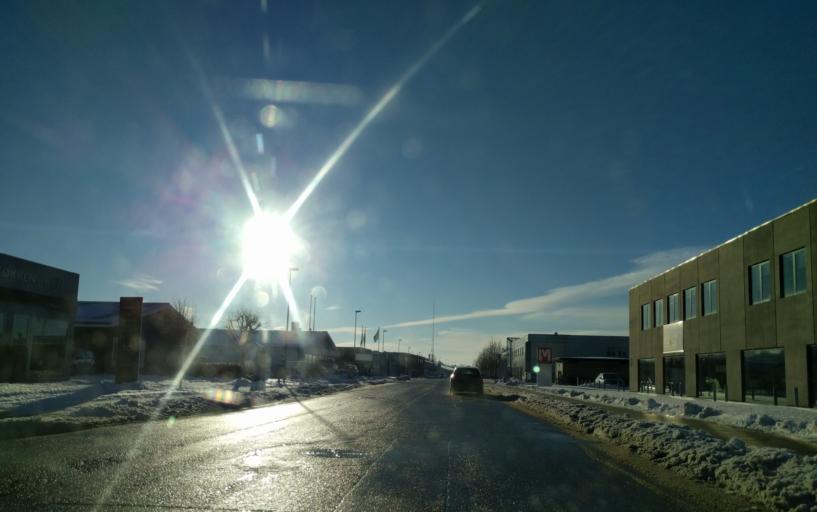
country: DK
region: North Denmark
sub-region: Alborg Kommune
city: Aalborg
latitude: 57.0371
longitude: 9.9270
